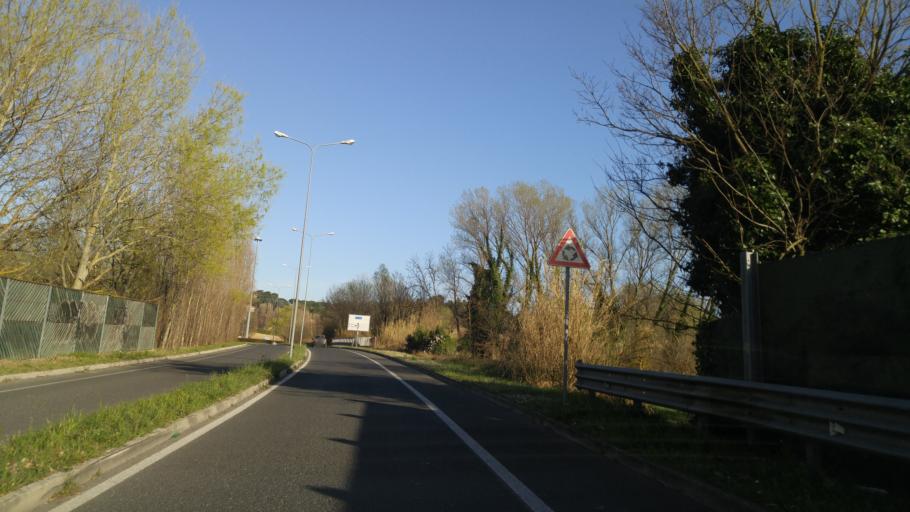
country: IT
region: The Marches
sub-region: Provincia di Pesaro e Urbino
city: Pesaro
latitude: 43.8879
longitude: 12.9047
